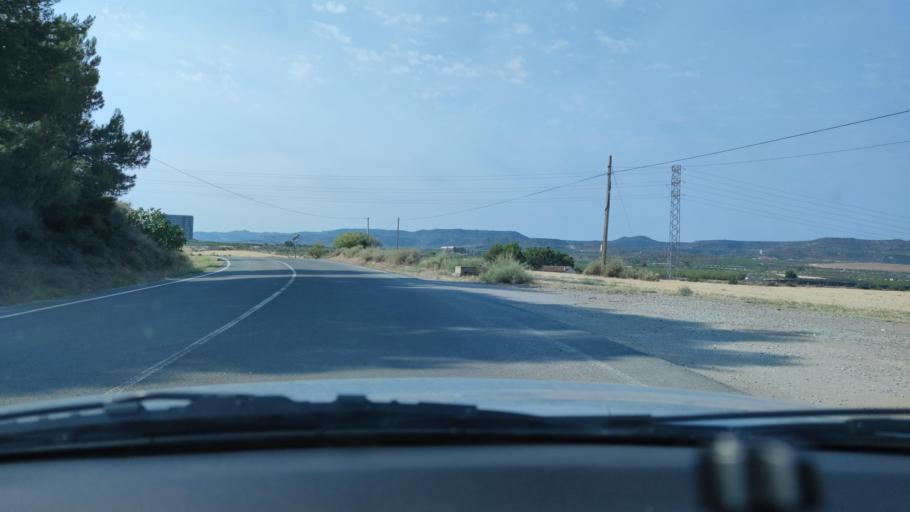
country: ES
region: Catalonia
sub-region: Provincia de Lleida
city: Juneda
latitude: 41.5093
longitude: 0.8717
